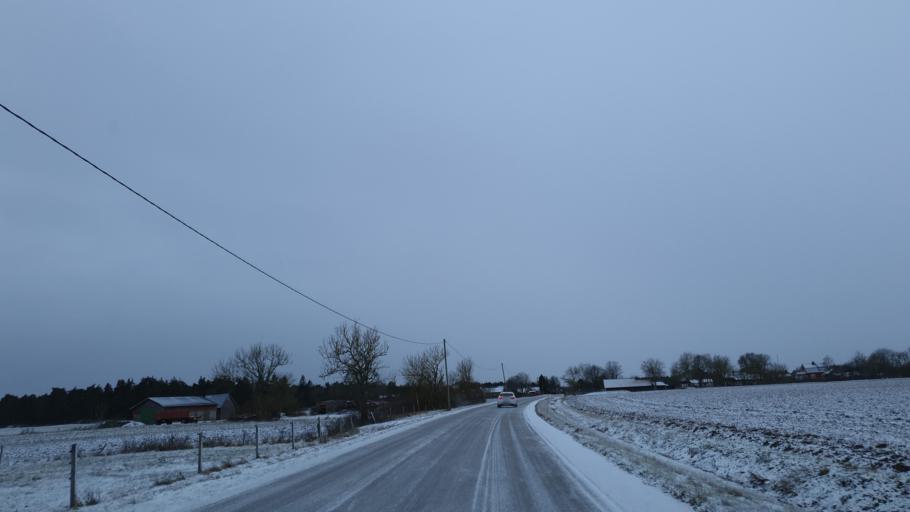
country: SE
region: Gotland
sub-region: Gotland
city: Visby
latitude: 57.4971
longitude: 18.5254
